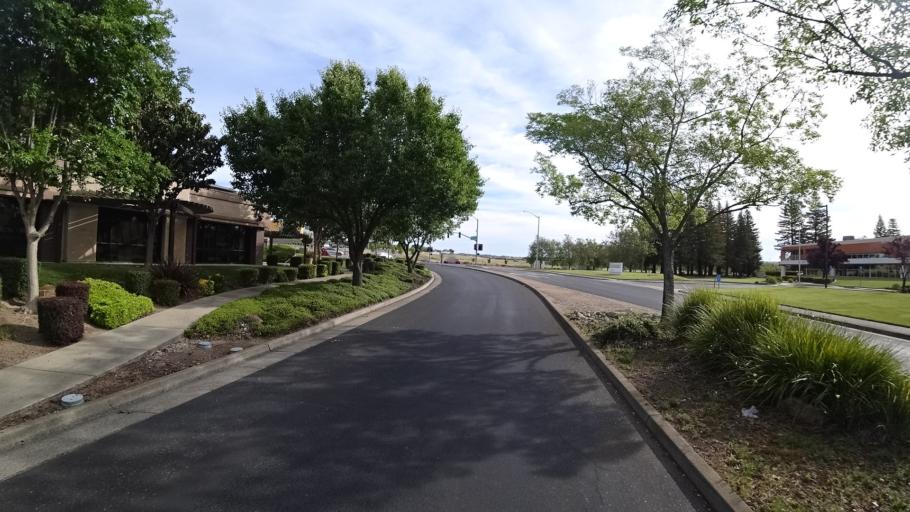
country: US
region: California
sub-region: Placer County
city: Rocklin
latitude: 38.8165
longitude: -121.2927
